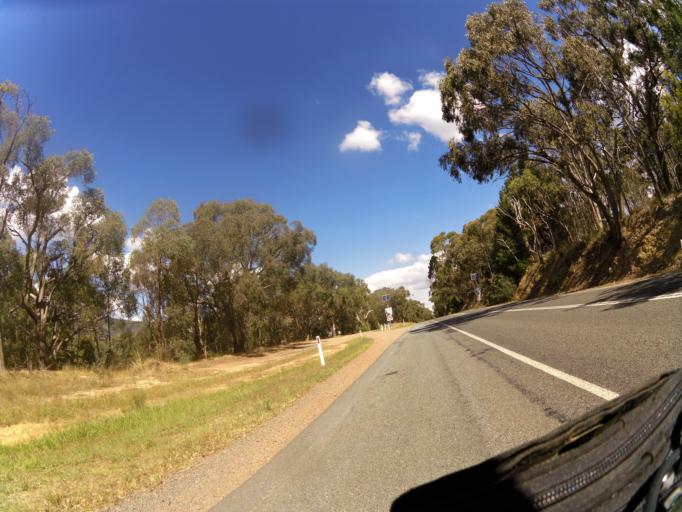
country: AU
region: Victoria
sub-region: Mansfield
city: Mansfield
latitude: -36.8395
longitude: 146.0073
